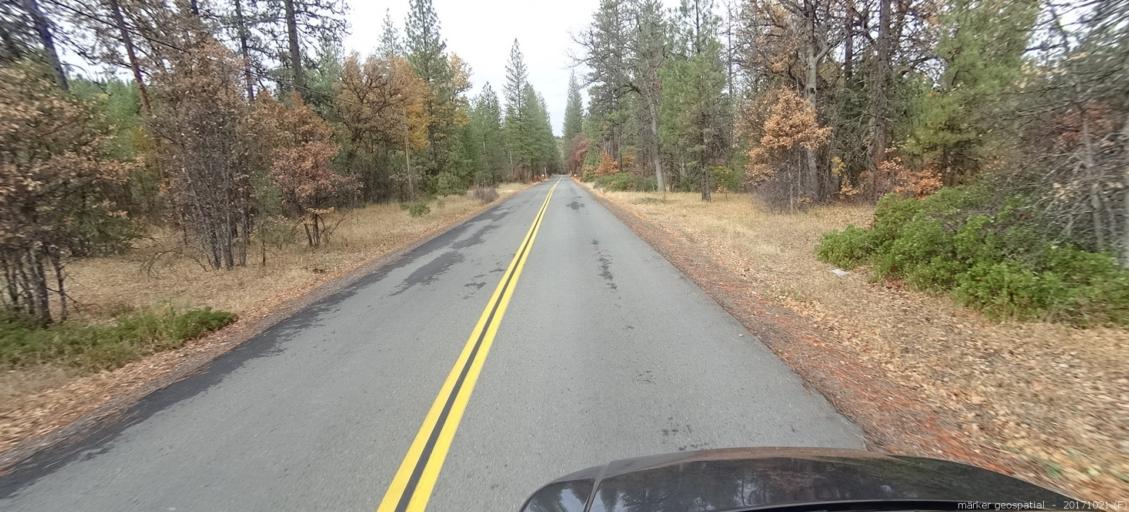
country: US
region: California
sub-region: Shasta County
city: Burney
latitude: 41.0036
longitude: -121.6418
